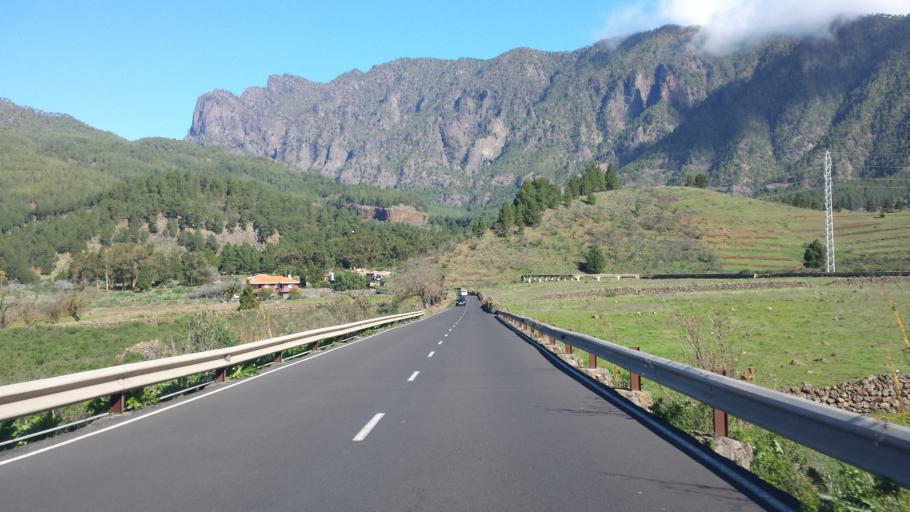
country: ES
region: Canary Islands
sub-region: Provincia de Santa Cruz de Tenerife
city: El Paso
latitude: 28.6572
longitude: -17.8521
